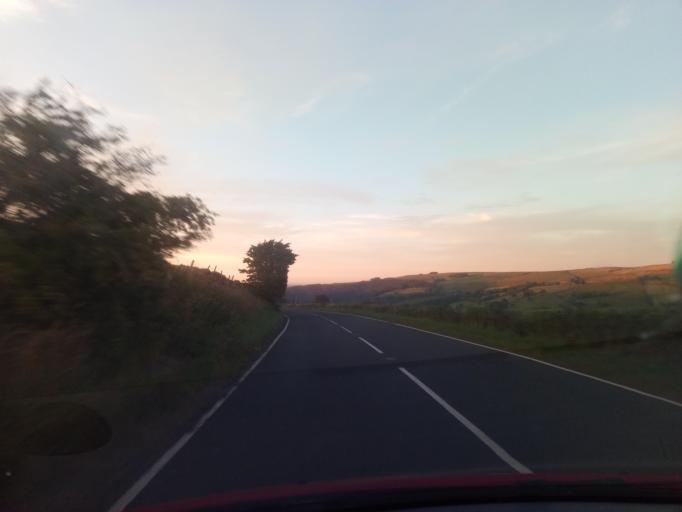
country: GB
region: England
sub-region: Northumberland
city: Bardon Mill
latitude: 54.8690
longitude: -2.3558
